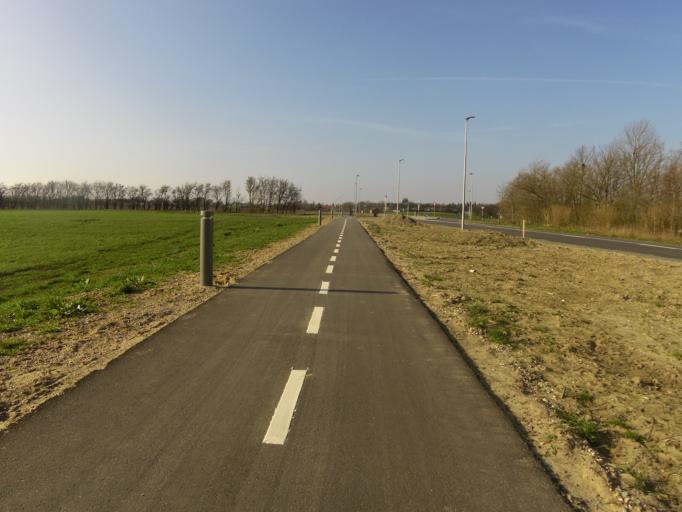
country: DK
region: South Denmark
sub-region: Vejen Kommune
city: Vejen
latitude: 55.4594
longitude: 9.1070
